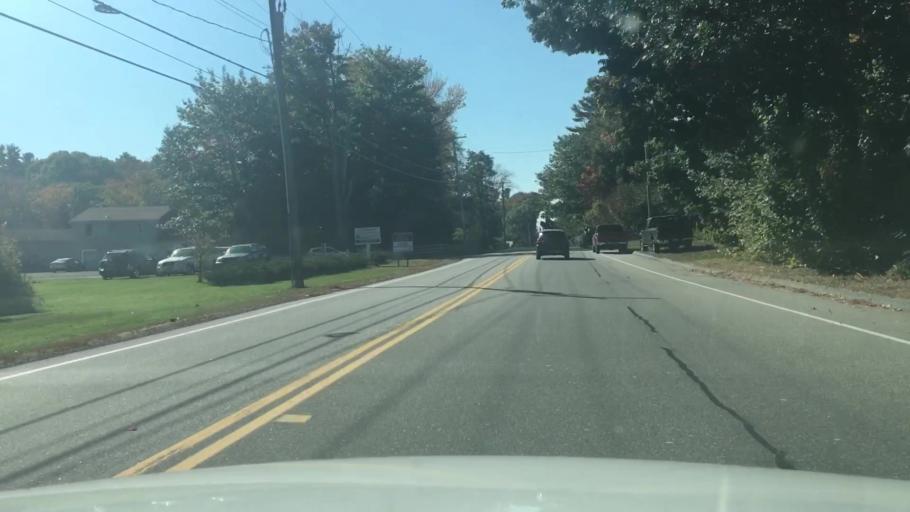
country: US
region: Maine
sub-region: Cumberland County
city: Westbrook
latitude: 43.6488
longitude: -70.3708
